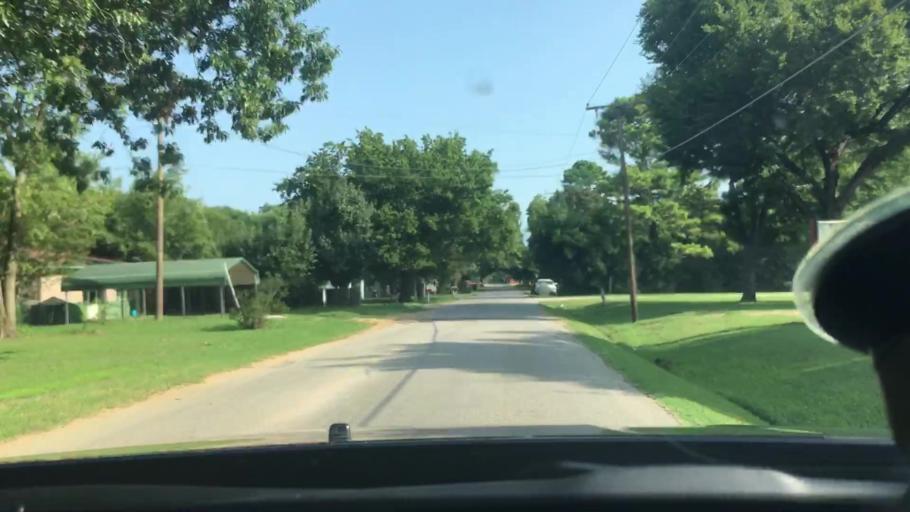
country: US
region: Oklahoma
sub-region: Johnston County
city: Tishomingo
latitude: 34.2274
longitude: -96.6711
